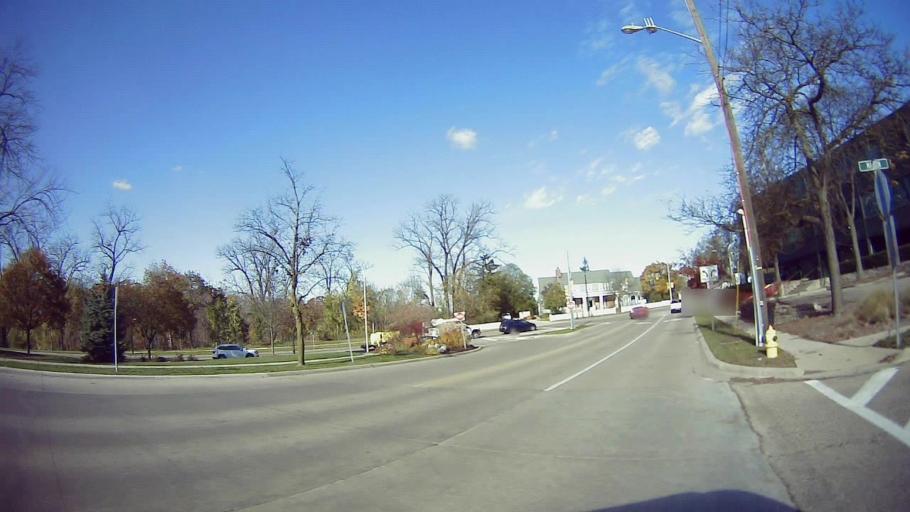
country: US
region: Michigan
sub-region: Oakland County
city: Birmingham
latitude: 42.5458
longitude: -83.2204
